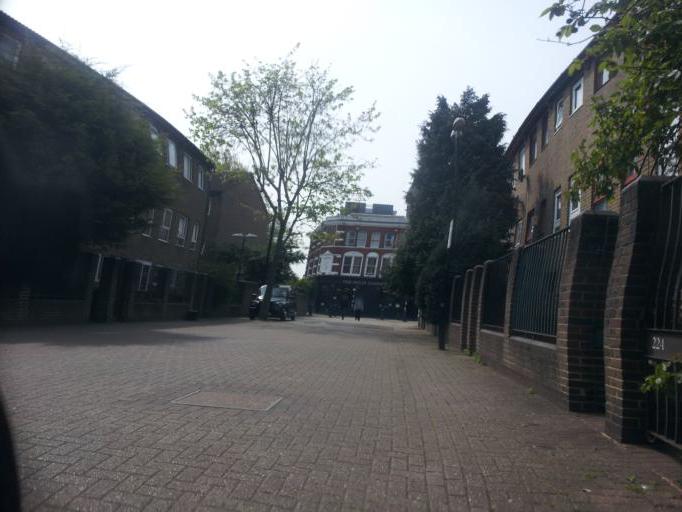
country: GB
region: England
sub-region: Greater London
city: Lambeth
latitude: 51.4921
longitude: -0.1176
